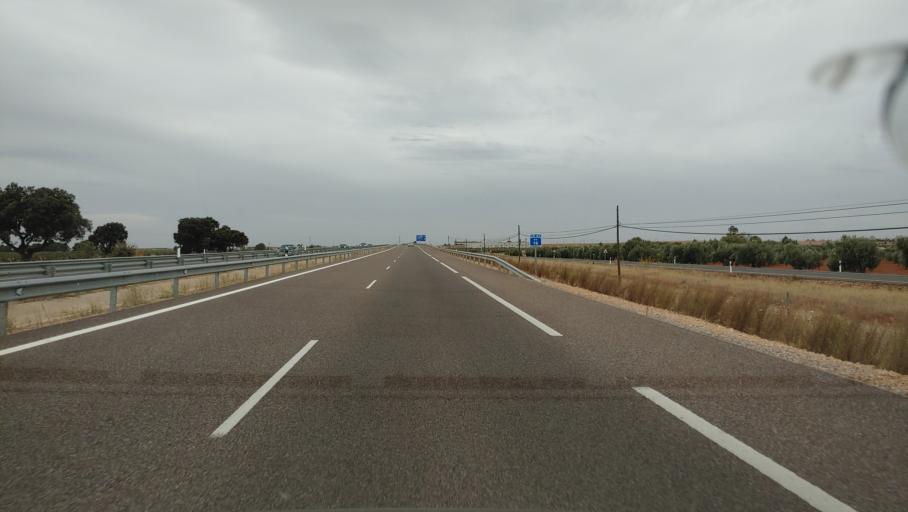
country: ES
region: Castille-La Mancha
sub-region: Provincia de Ciudad Real
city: Valenzuela de Calatrava
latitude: 38.9011
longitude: -3.7949
